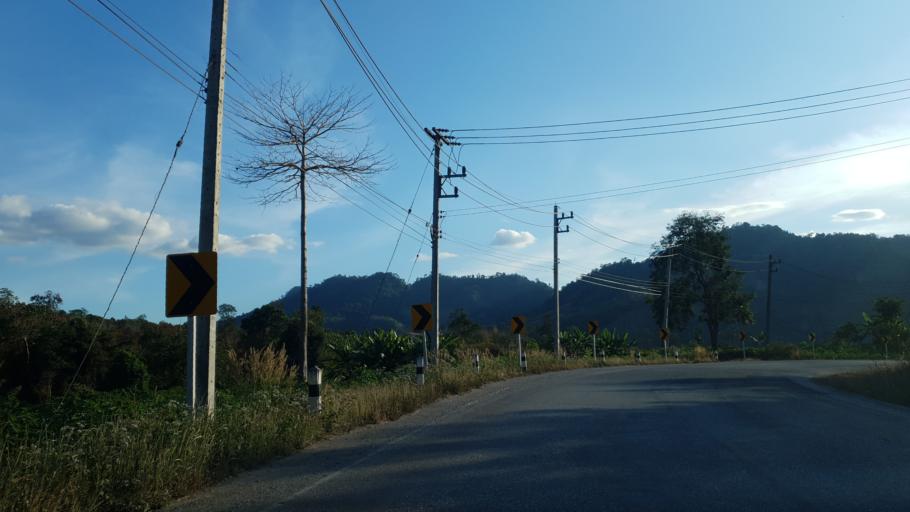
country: TH
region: Loei
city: Dan Sai
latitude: 17.2270
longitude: 101.0743
